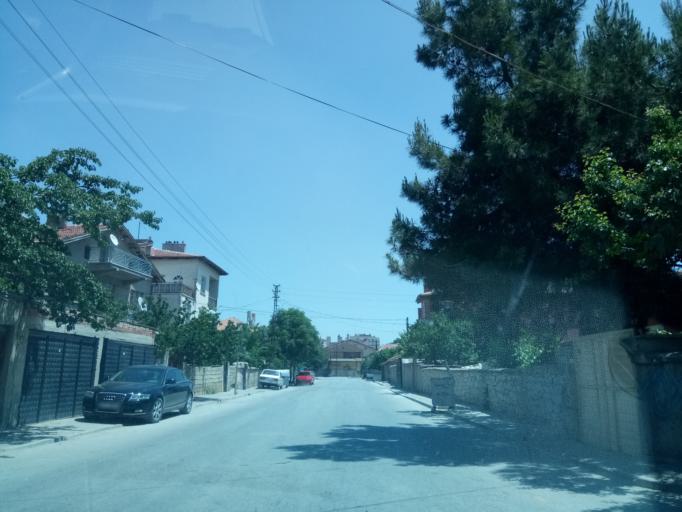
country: TR
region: Konya
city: Konya
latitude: 37.8468
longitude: 32.4966
